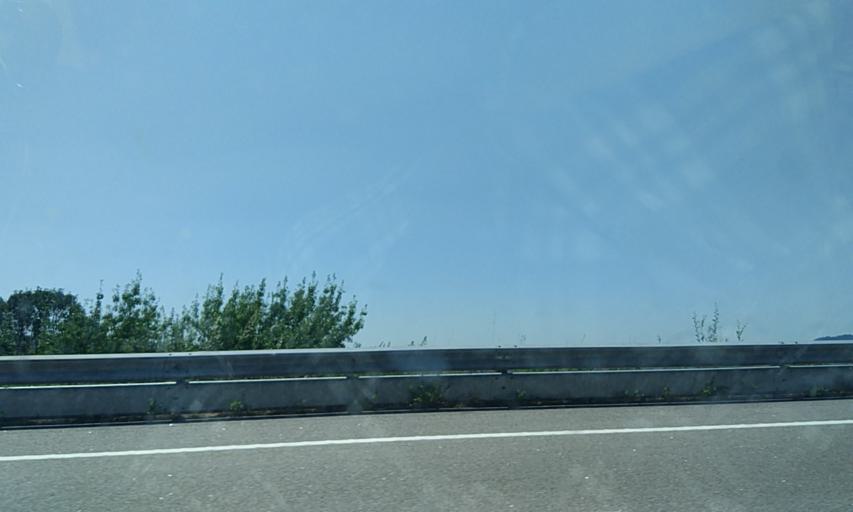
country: PT
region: Braganca
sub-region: Macedo de Cavaleiros
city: Macedo de Cavaleiros
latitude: 41.5946
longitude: -6.9101
